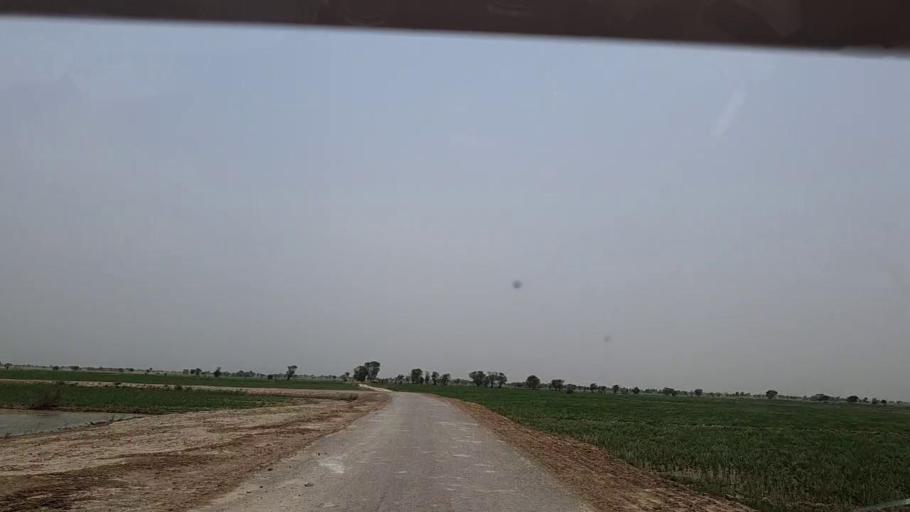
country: PK
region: Sindh
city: Khairpur Nathan Shah
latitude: 27.0171
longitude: 67.6507
